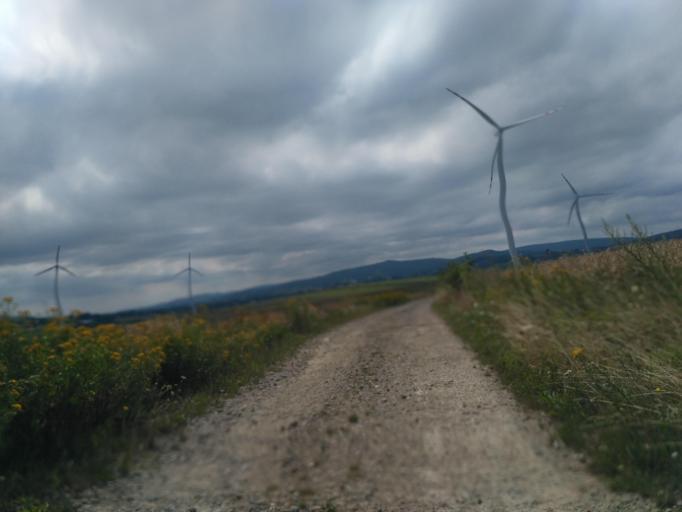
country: PL
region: Subcarpathian Voivodeship
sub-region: Powiat krosnienski
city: Rymanow
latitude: 49.6037
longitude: 21.8475
